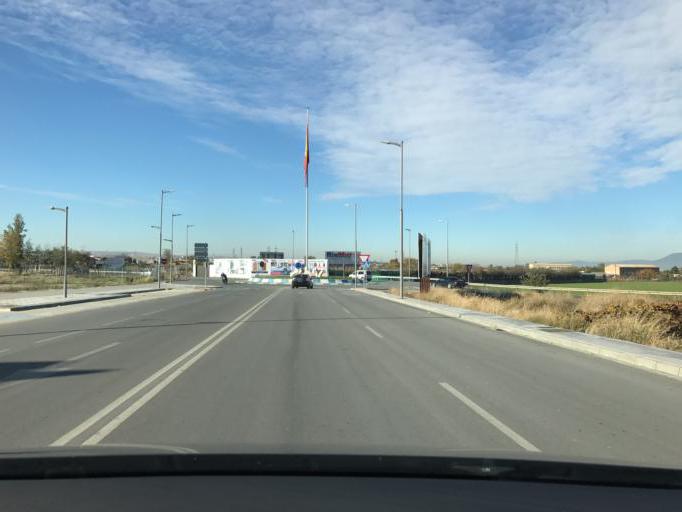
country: ES
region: Andalusia
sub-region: Provincia de Granada
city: Churriana de la Vega
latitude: 37.1507
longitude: -3.6519
